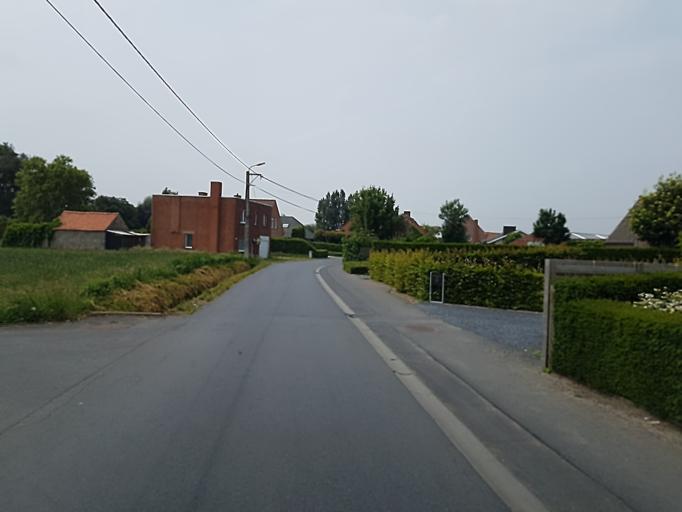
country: BE
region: Flanders
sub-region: Provincie West-Vlaanderen
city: Izegem
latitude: 50.9451
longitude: 3.2090
